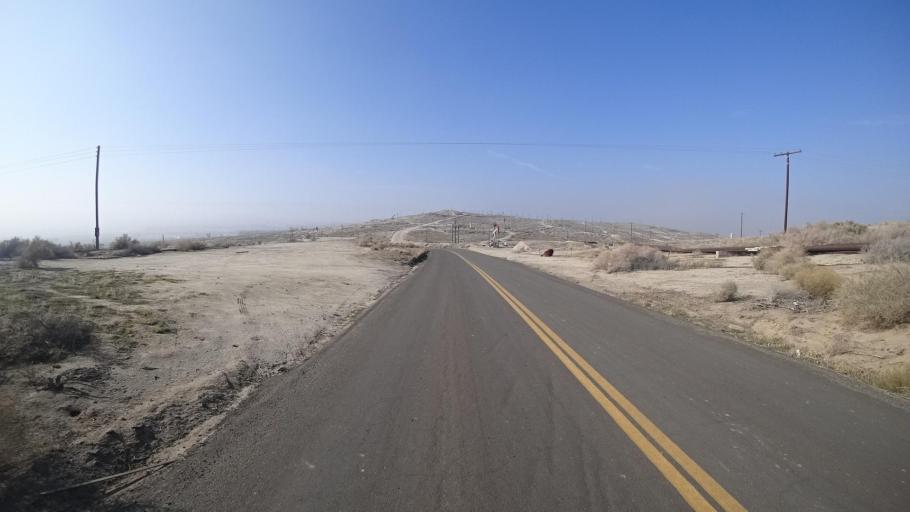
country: US
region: California
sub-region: Kern County
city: Ford City
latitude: 35.1635
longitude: -119.4187
